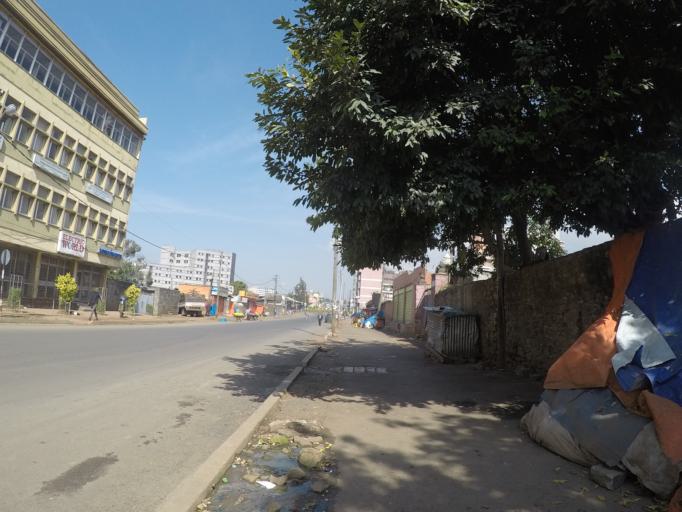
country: ET
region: Adis Abeba
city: Addis Ababa
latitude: 9.0315
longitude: 38.7490
